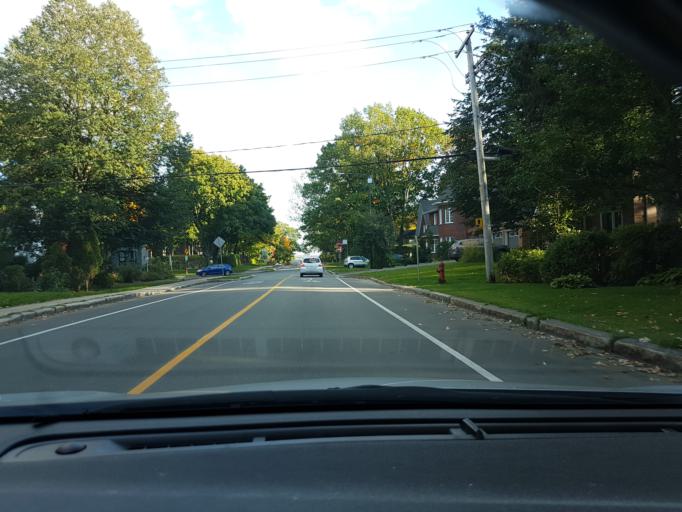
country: CA
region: Quebec
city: Quebec
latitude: 46.7723
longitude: -71.2704
